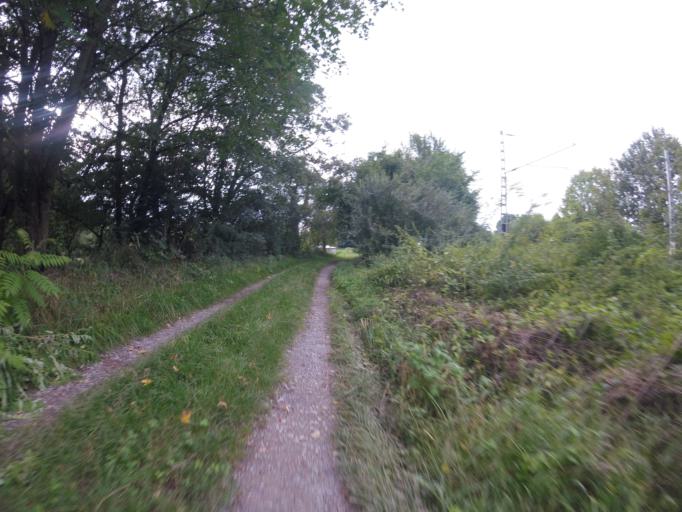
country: DE
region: Baden-Wuerttemberg
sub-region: Regierungsbezirk Stuttgart
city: Mittelschontal
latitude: 48.9320
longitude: 9.4118
